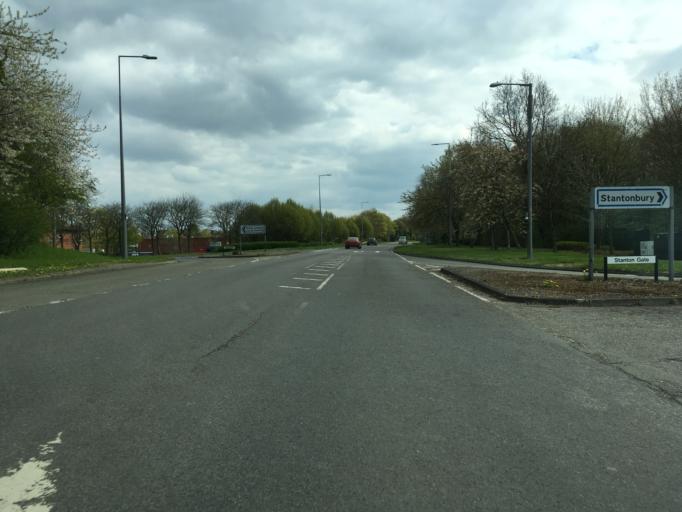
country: GB
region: England
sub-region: Milton Keynes
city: Milton Keynes
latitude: 52.0667
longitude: -0.7616
